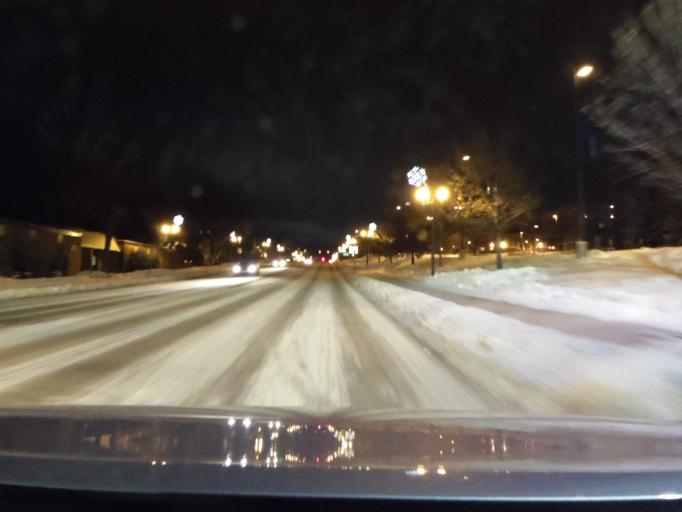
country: US
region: Wisconsin
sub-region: Dunn County
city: Menomonie
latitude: 44.8739
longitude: -91.9297
